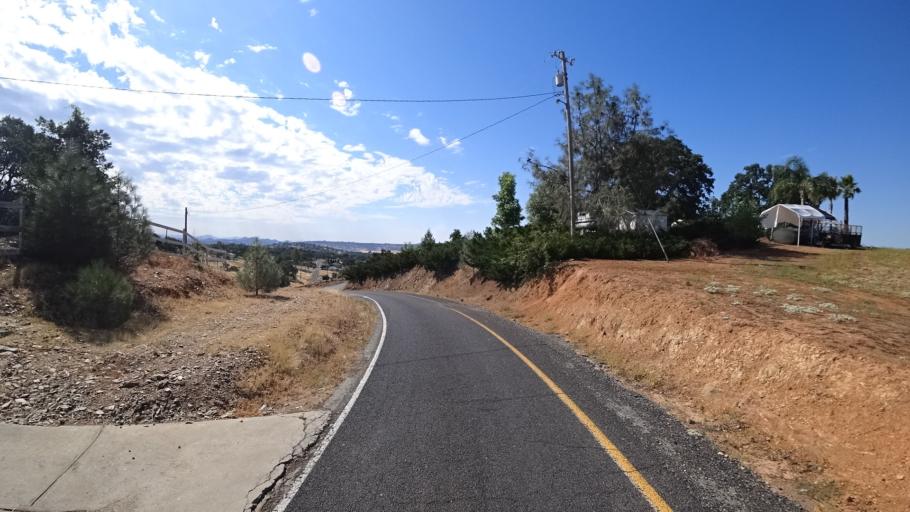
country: US
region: California
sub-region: Calaveras County
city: Copperopolis
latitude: 37.9249
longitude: -120.6333
